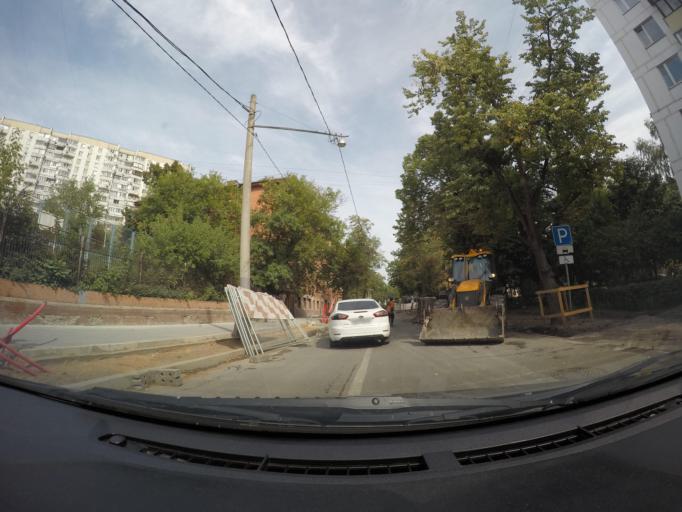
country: RU
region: Moscow
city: Sokol'niki
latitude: 55.7875
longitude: 37.6827
